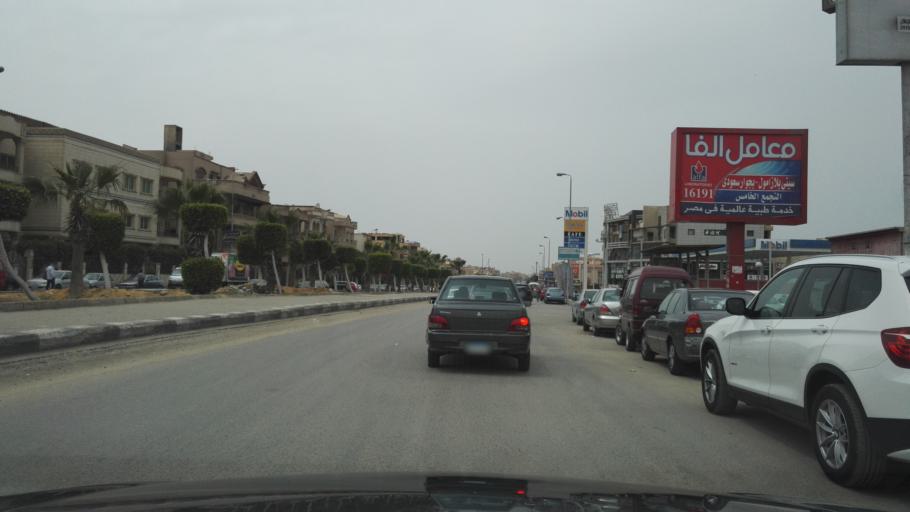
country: EG
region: Muhafazat al Qahirah
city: Cairo
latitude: 30.0023
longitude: 31.4228
